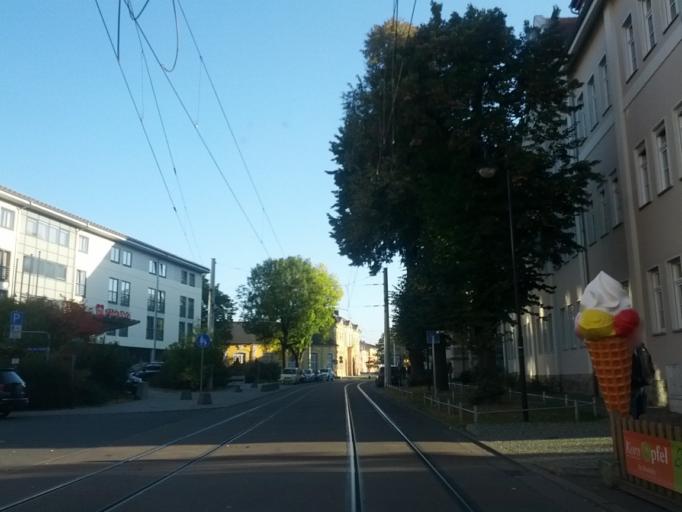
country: DE
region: Thuringia
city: Gera
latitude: 50.8840
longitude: 12.0693
